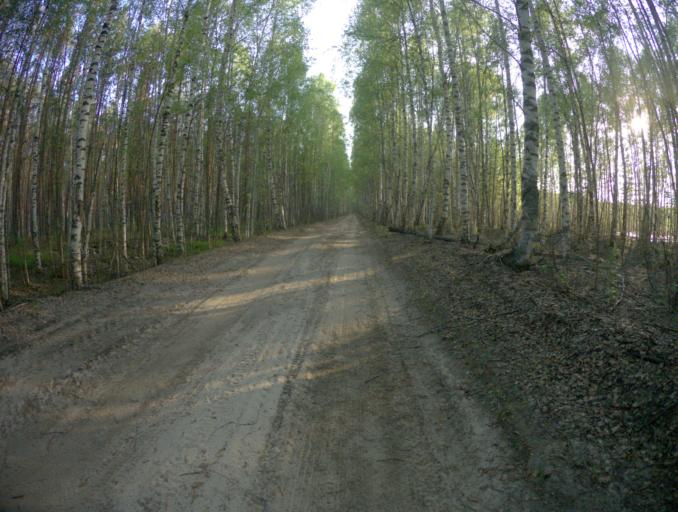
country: RU
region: Vladimir
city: Vyazniki
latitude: 56.3662
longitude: 42.1533
